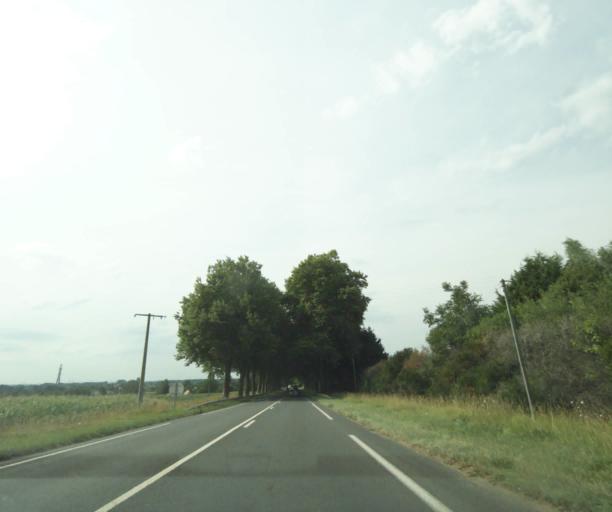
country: FR
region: Pays de la Loire
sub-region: Departement de la Sarthe
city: Laigne-en-Belin
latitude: 47.8870
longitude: 0.2468
